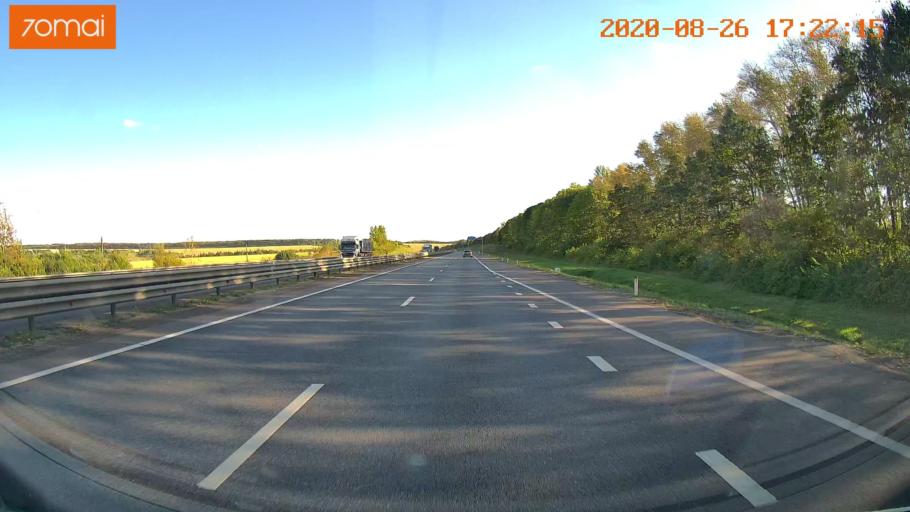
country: RU
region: Tula
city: Volovo
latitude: 53.5528
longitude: 38.1125
